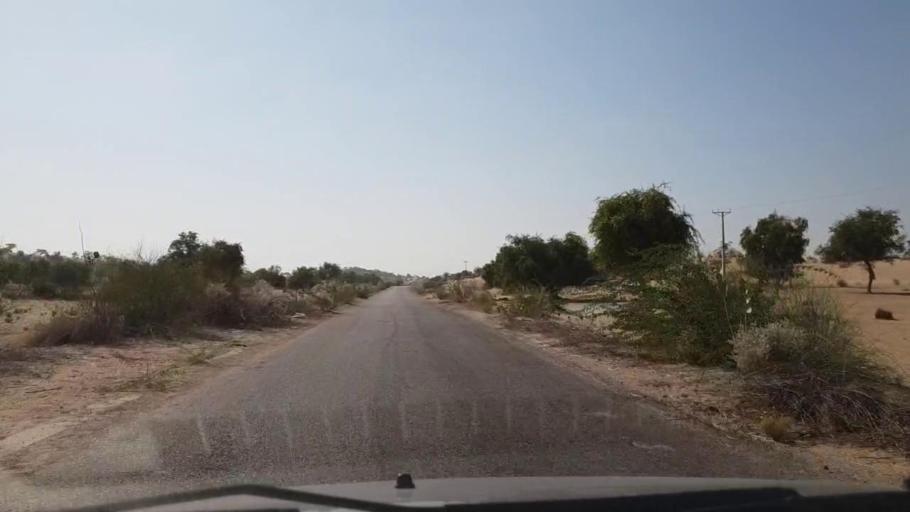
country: PK
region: Sindh
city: Diplo
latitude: 24.5627
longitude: 69.6729
